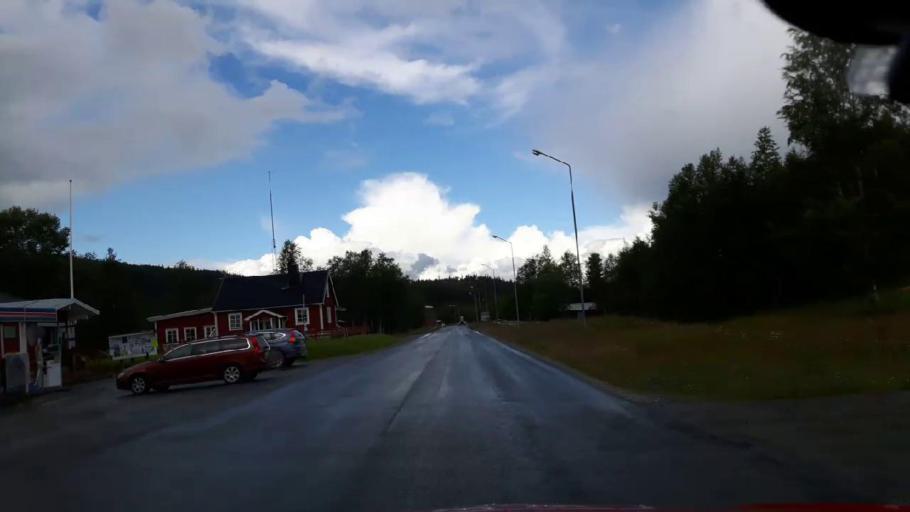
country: SE
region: Vaesterbotten
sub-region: Vilhelmina Kommun
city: Sjoberg
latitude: 64.9716
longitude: 15.3383
